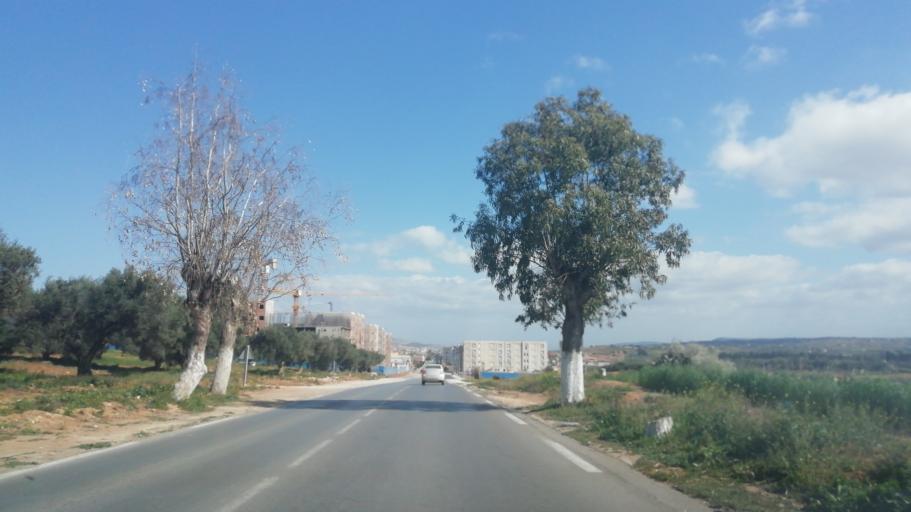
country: DZ
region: Mostaganem
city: Mostaganem
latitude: 35.9998
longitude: 0.3279
